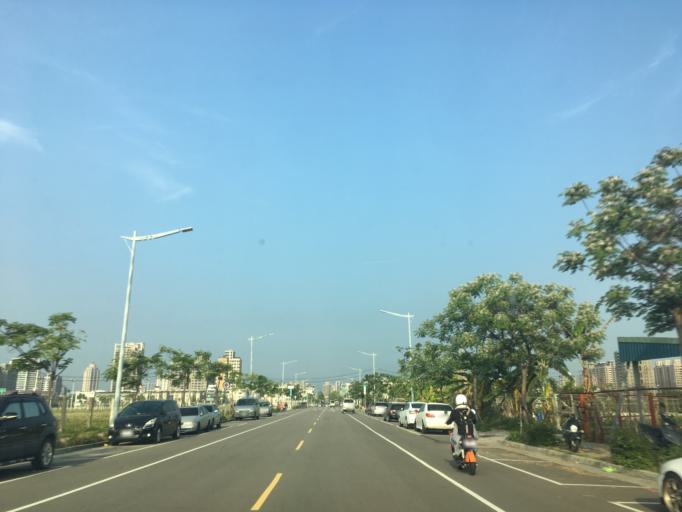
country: TW
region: Taiwan
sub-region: Taichung City
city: Taichung
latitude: 24.1905
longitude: 120.6959
